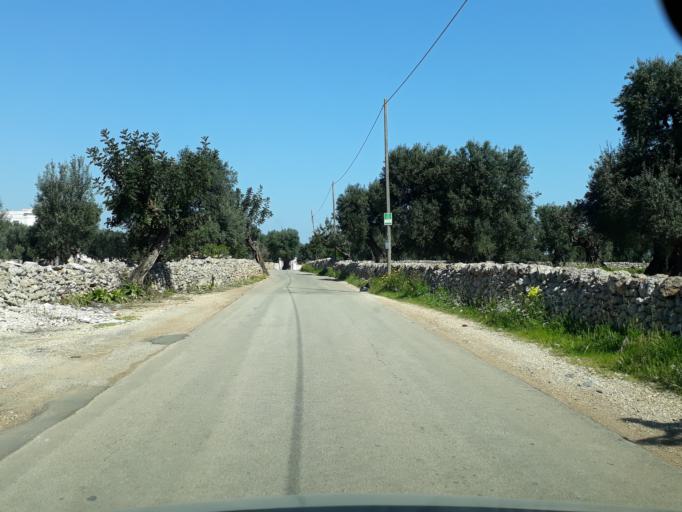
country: IT
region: Apulia
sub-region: Provincia di Brindisi
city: Fasano
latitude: 40.8315
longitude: 17.3779
